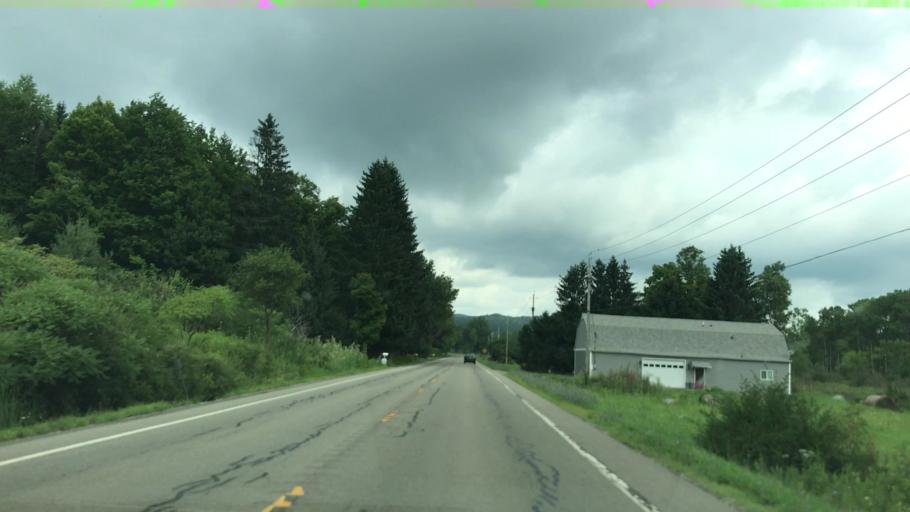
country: US
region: New York
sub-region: Steuben County
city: Bath
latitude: 42.3973
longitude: -77.3485
